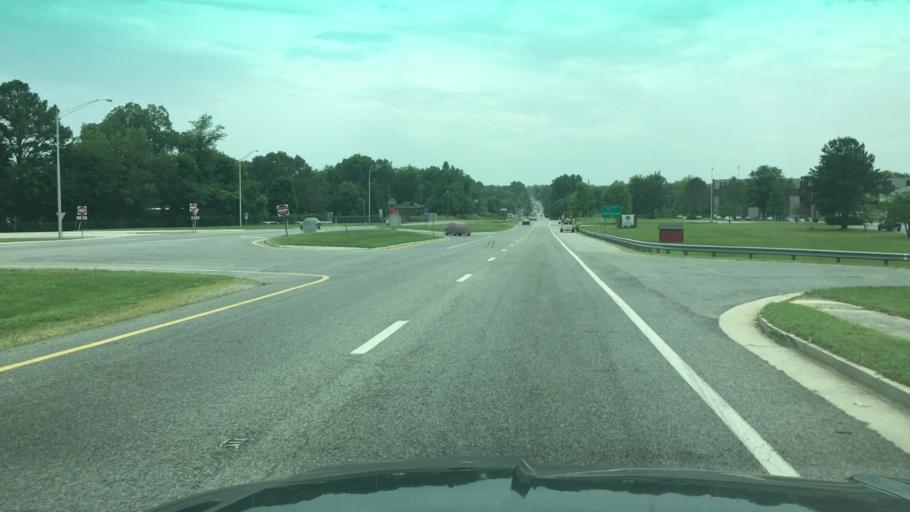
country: US
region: Tennessee
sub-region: Coffee County
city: Manchester
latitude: 35.4887
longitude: -86.0748
